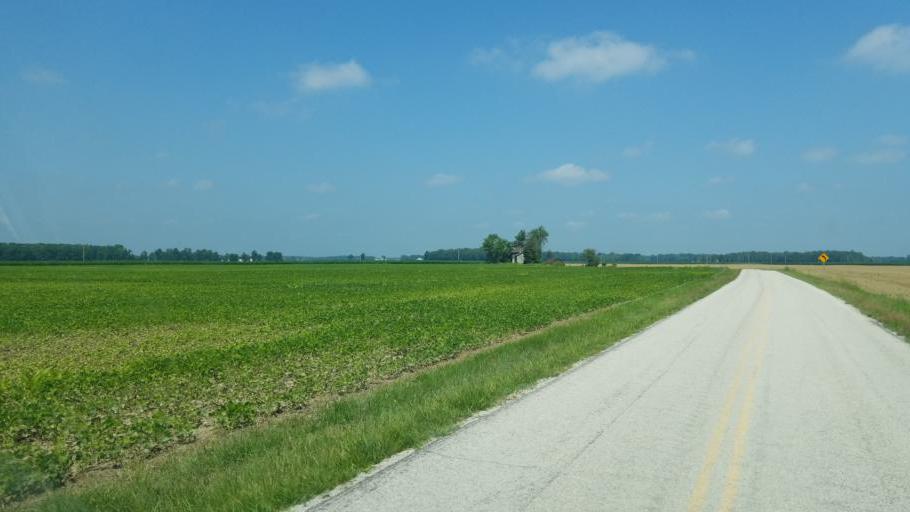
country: US
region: Ohio
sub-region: Huron County
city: Willard
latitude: 40.9821
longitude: -82.8770
